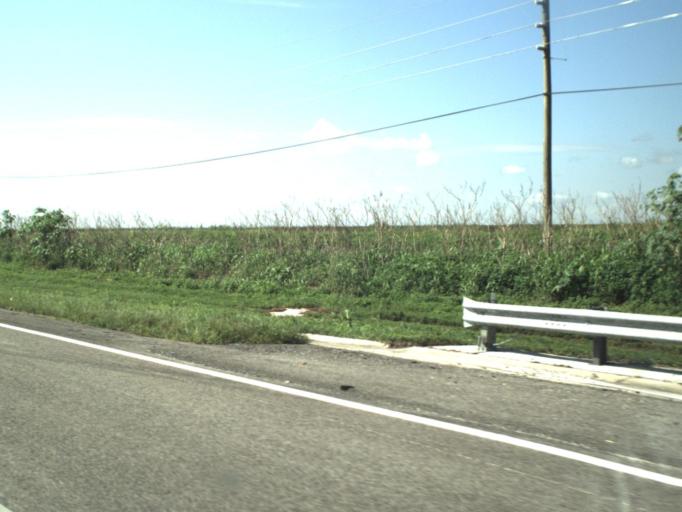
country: US
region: Florida
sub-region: Palm Beach County
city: Belle Glade Camp
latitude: 26.3959
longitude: -80.5851
